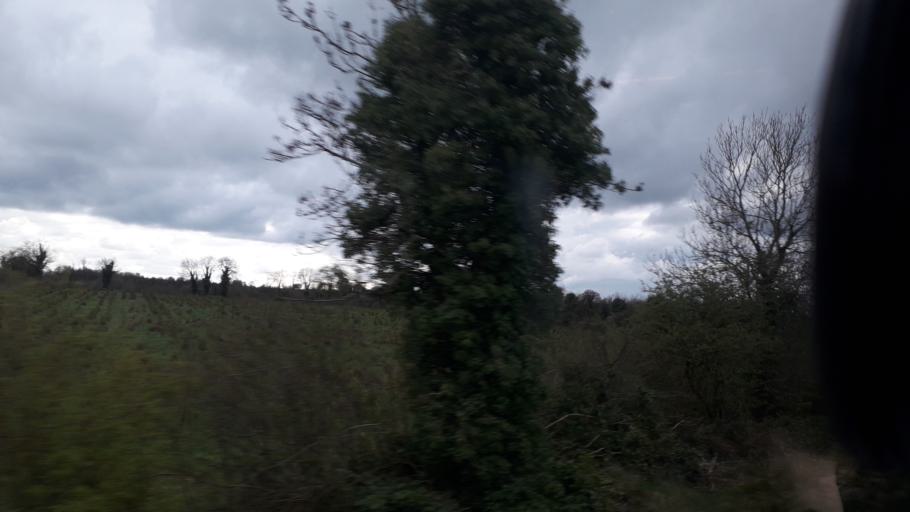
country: IE
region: Leinster
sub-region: An Longfort
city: Edgeworthstown
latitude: 53.6952
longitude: -7.6388
